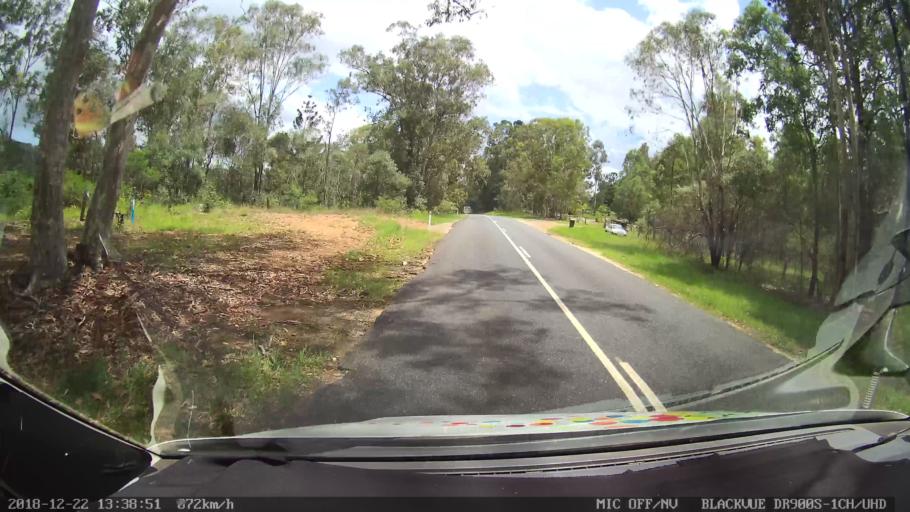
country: AU
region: New South Wales
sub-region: Clarence Valley
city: Coutts Crossing
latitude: -29.9047
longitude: 152.7862
